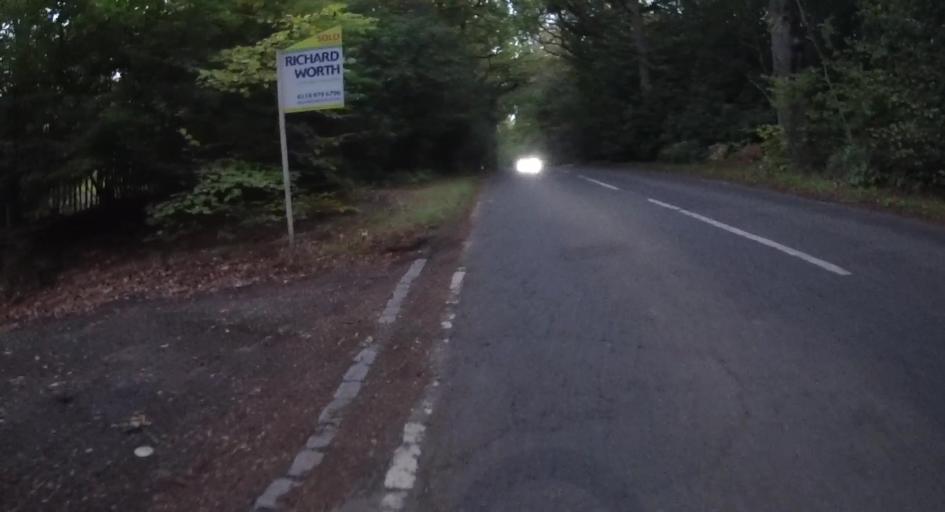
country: GB
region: England
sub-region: Hampshire
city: Eversley
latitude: 51.3595
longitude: -0.8781
